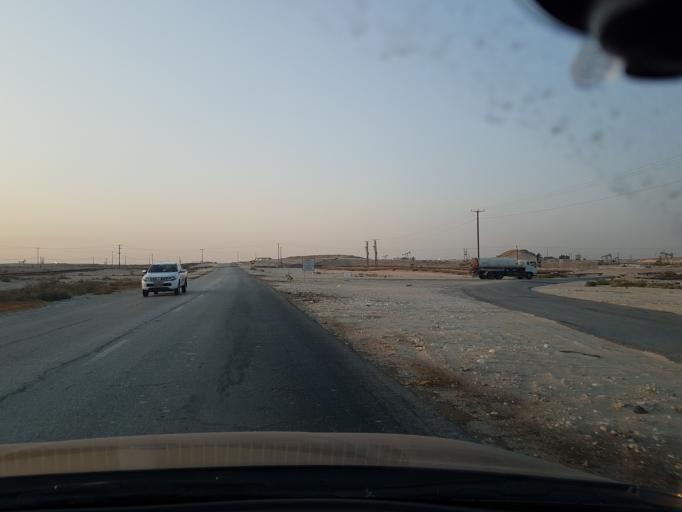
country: BH
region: Central Governorate
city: Dar Kulayb
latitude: 26.0527
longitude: 50.5566
